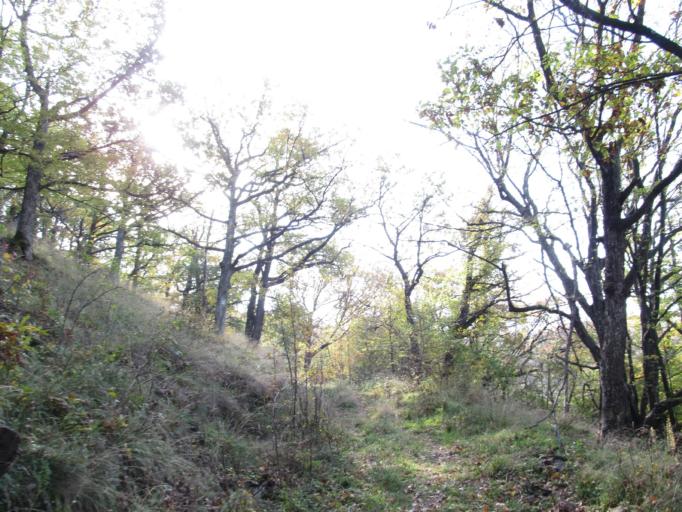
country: SK
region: Nitriansky
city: Sahy
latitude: 47.9800
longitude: 18.9042
